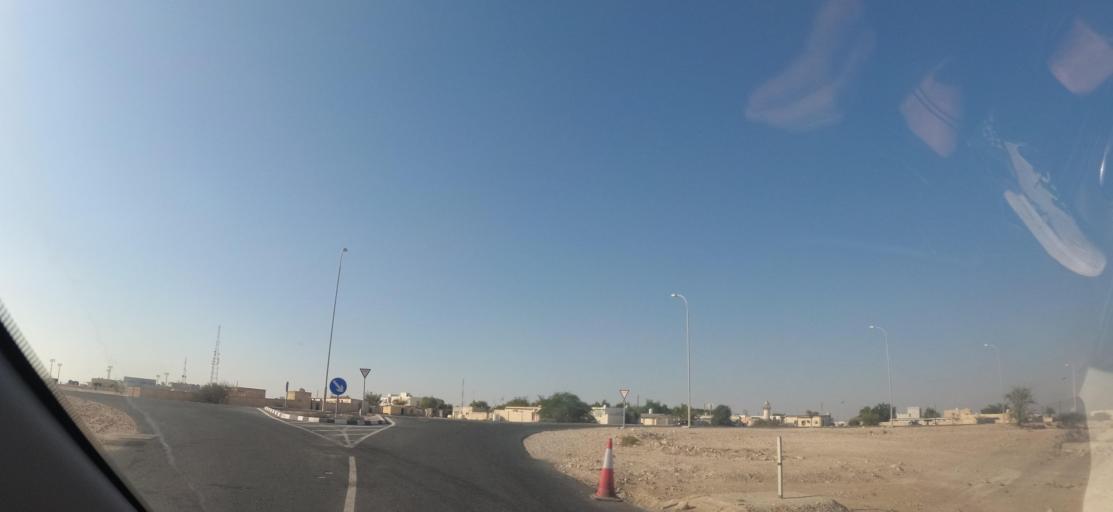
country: QA
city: Al Jumayliyah
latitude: 25.6188
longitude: 51.0859
